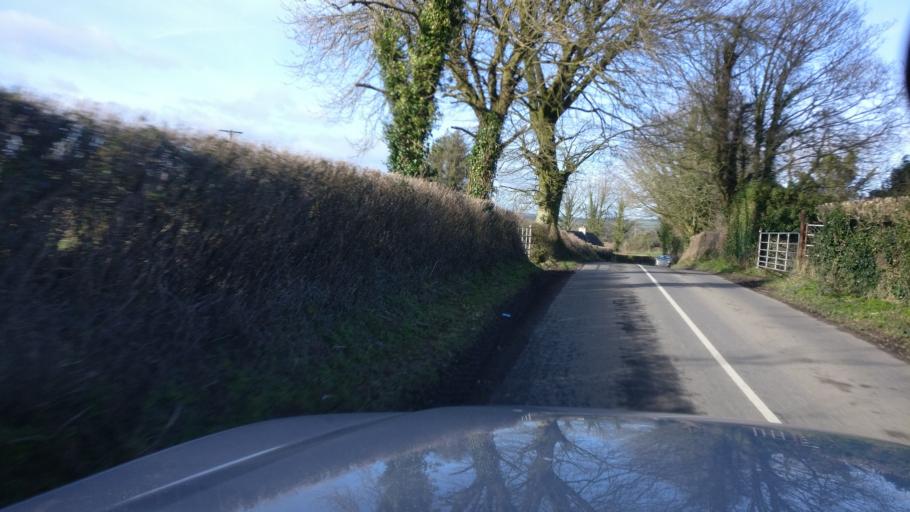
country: IE
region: Leinster
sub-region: Kilkenny
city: Castlecomer
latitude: 52.8784
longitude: -7.1629
